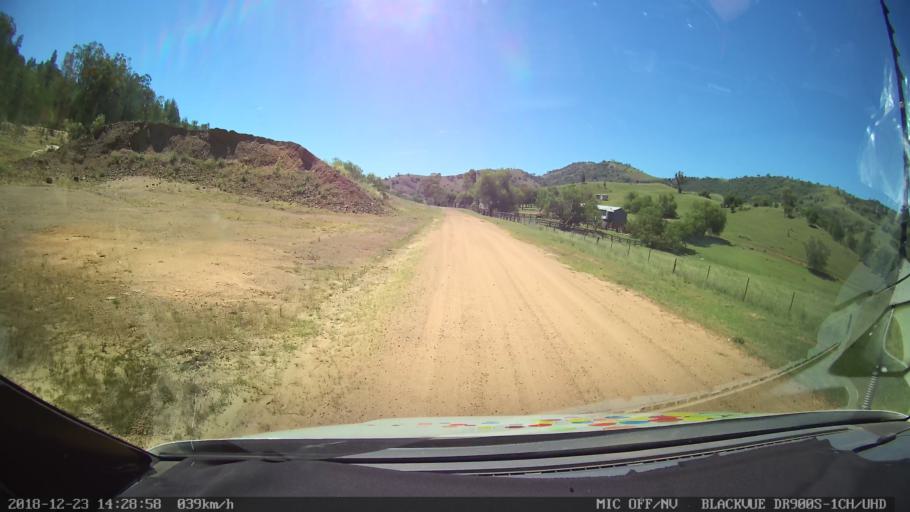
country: AU
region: New South Wales
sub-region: Tamworth Municipality
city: Manilla
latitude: -30.6114
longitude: 150.9396
